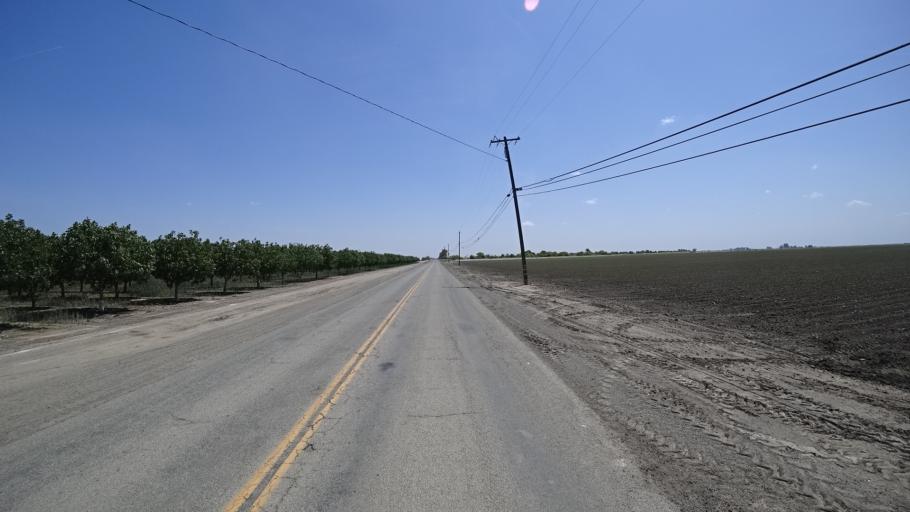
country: US
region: California
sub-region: Kings County
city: Stratford
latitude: 36.1894
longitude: -119.8510
